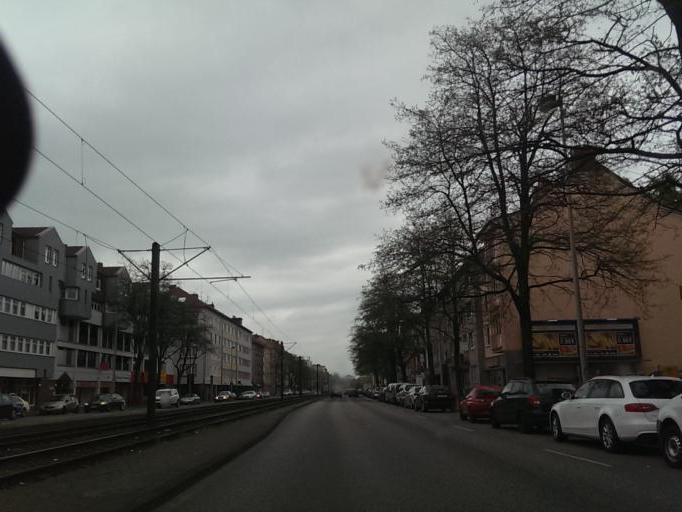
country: DE
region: Lower Saxony
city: Hannover
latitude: 52.3916
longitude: 9.7349
